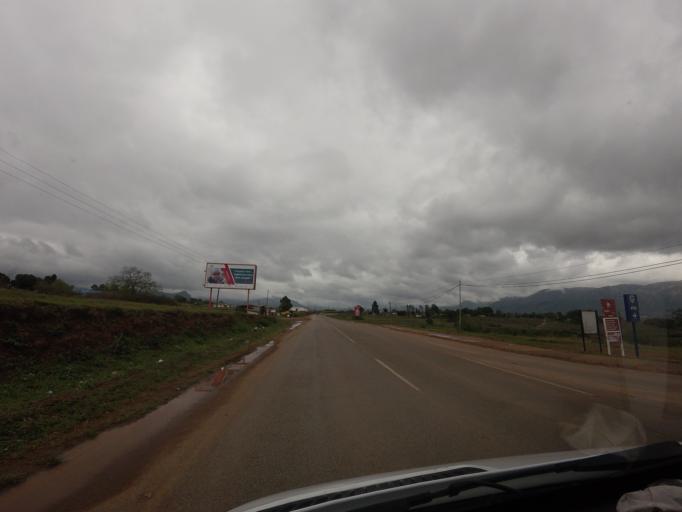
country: SZ
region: Hhohho
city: Lobamba
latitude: -26.4888
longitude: 31.2238
